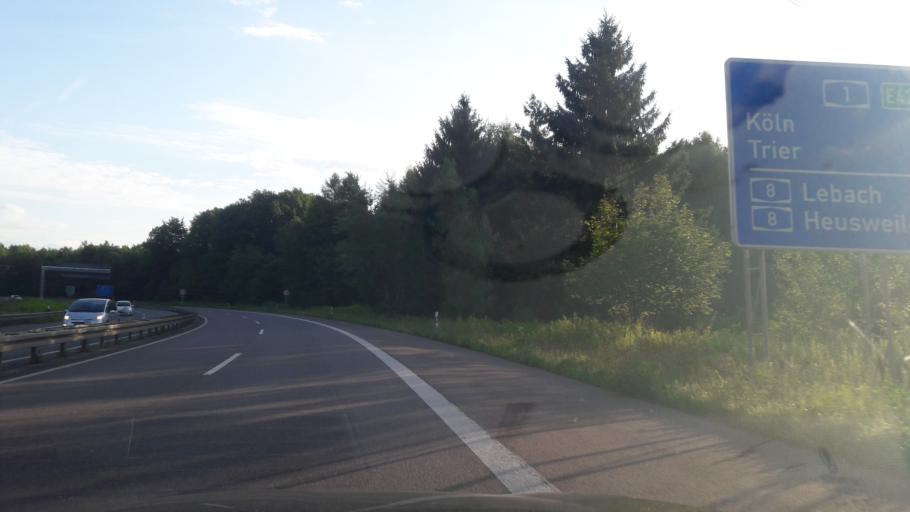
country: DE
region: Saarland
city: Saarbrucken
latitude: 49.2652
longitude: 6.9617
